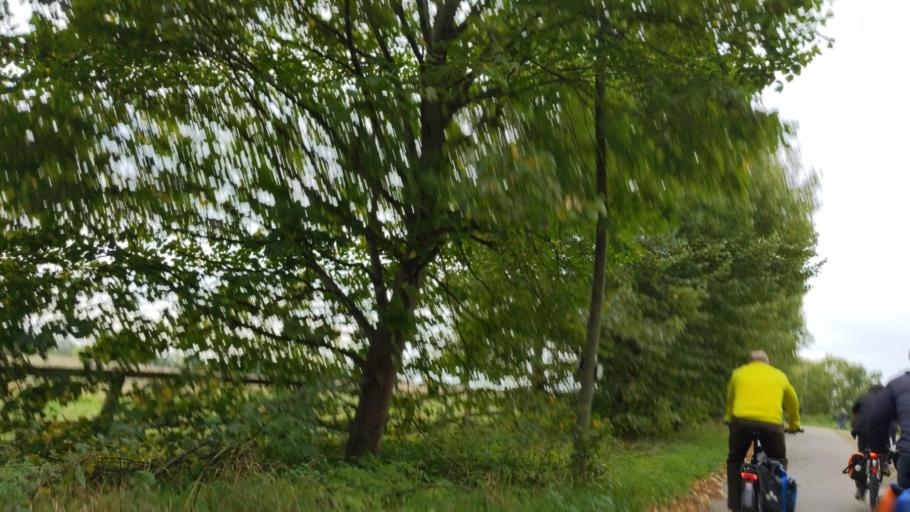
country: DE
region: Schleswig-Holstein
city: Gross Gronau
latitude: 53.8013
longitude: 10.7587
